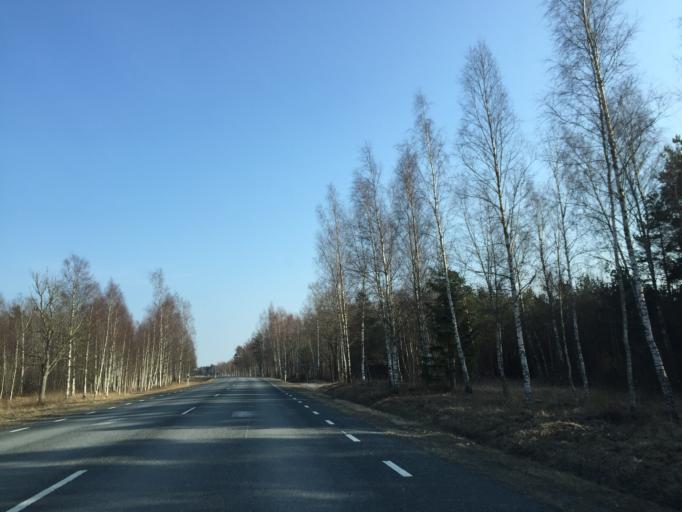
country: EE
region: Saare
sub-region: Orissaare vald
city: Orissaare
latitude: 58.5837
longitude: 23.3505
